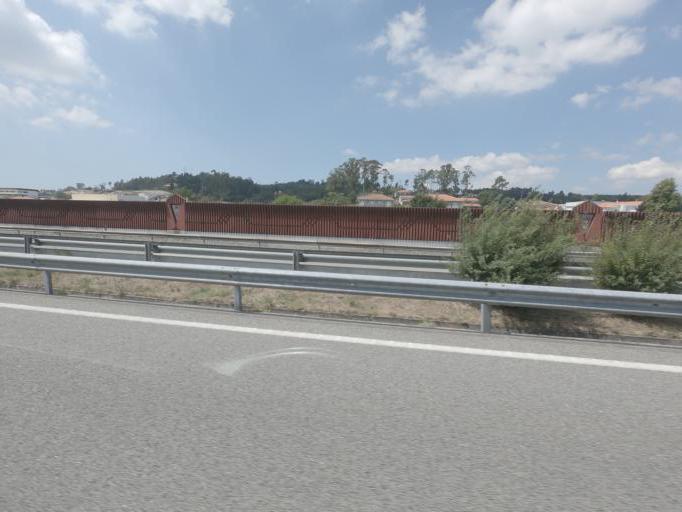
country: PT
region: Porto
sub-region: Lousada
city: Meinedo
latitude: 41.2256
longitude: -8.2325
